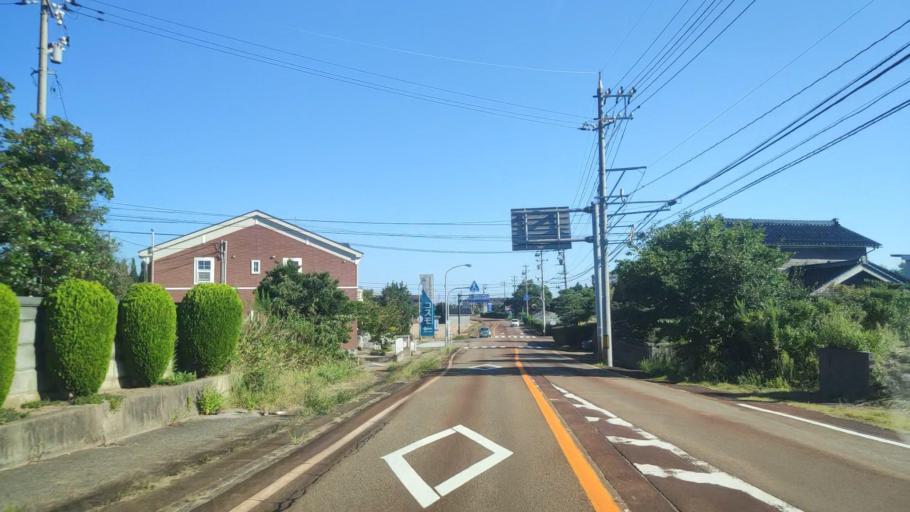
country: JP
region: Ishikawa
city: Hakui
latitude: 36.8690
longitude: 136.7726
